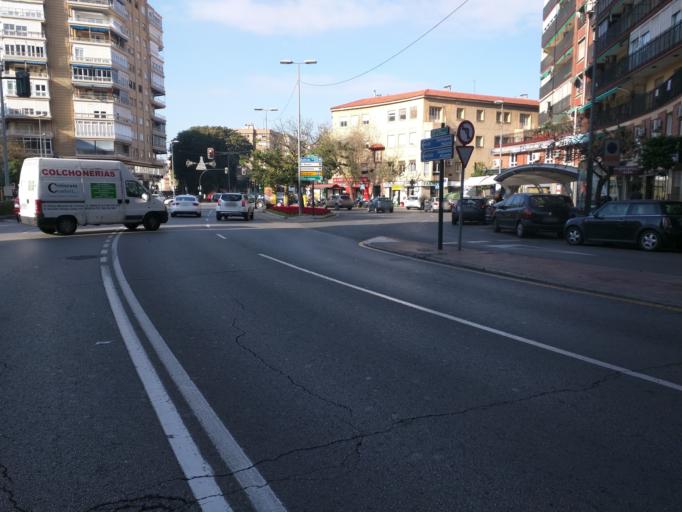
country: ES
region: Murcia
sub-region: Murcia
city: Murcia
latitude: 37.9913
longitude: -1.1348
